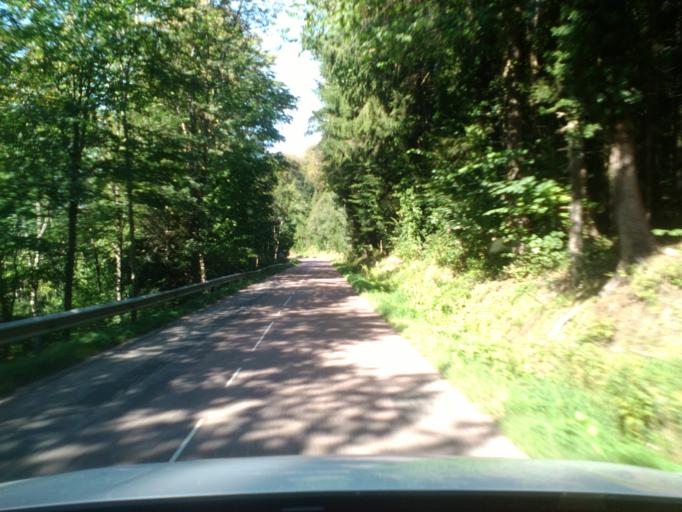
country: FR
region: Lorraine
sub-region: Departement des Vosges
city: Senones
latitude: 48.3375
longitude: 7.0056
